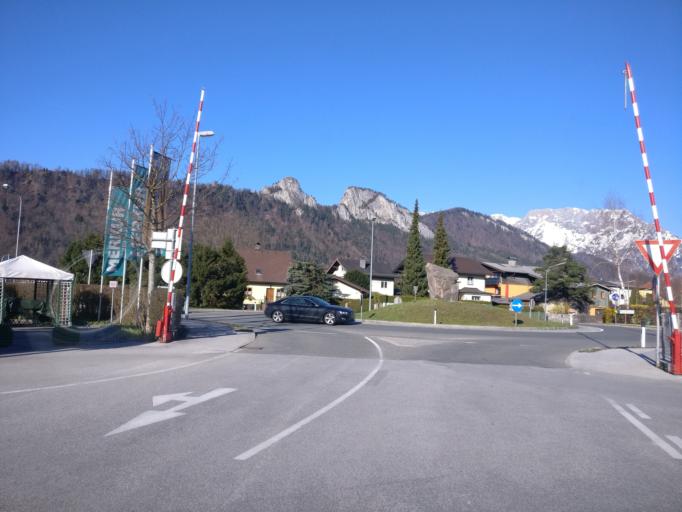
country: AT
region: Salzburg
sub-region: Politischer Bezirk Hallein
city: Hallein
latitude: 47.6905
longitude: 13.1004
